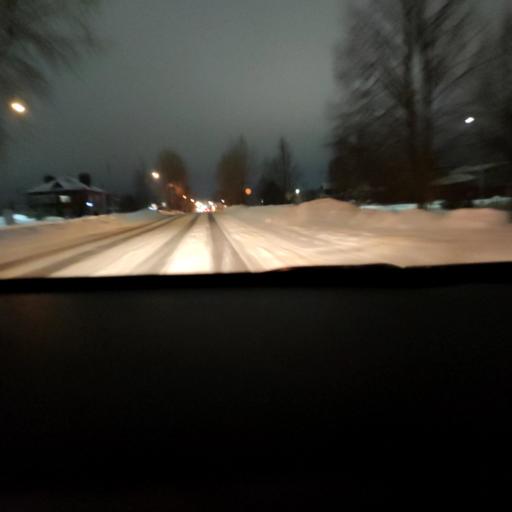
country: RU
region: Tatarstan
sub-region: Chistopol'skiy Rayon
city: Chistopol'
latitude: 55.3565
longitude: 50.6559
